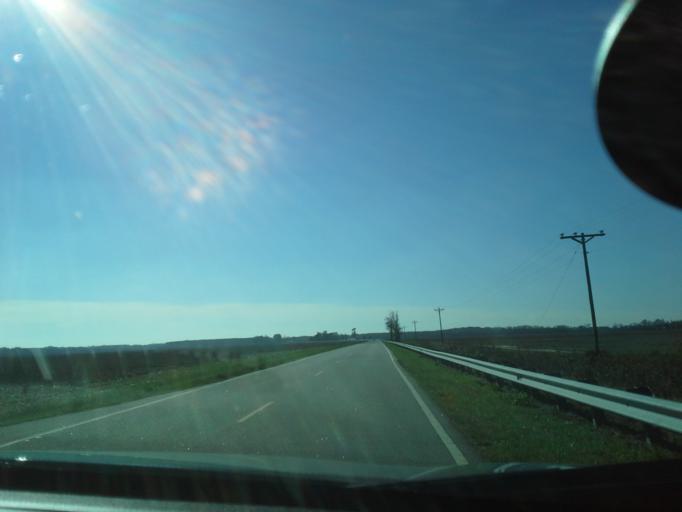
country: US
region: North Carolina
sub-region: Beaufort County
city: Belhaven
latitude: 35.6176
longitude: -76.6472
